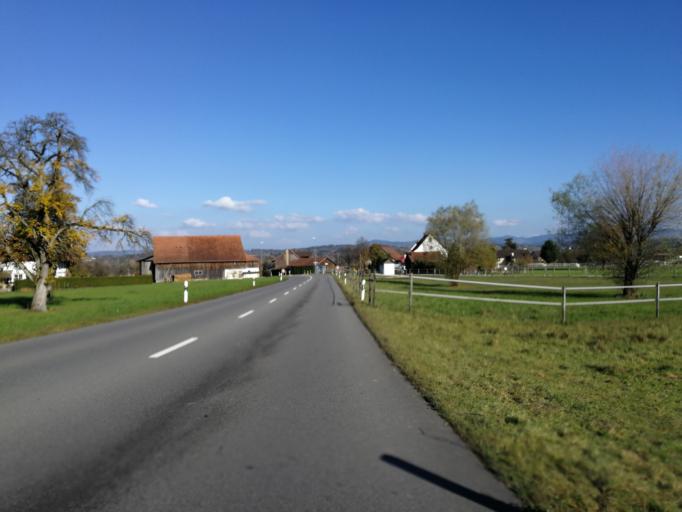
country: CH
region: Zurich
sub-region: Bezirk Uster
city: Hinteregg
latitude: 47.3165
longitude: 8.6966
